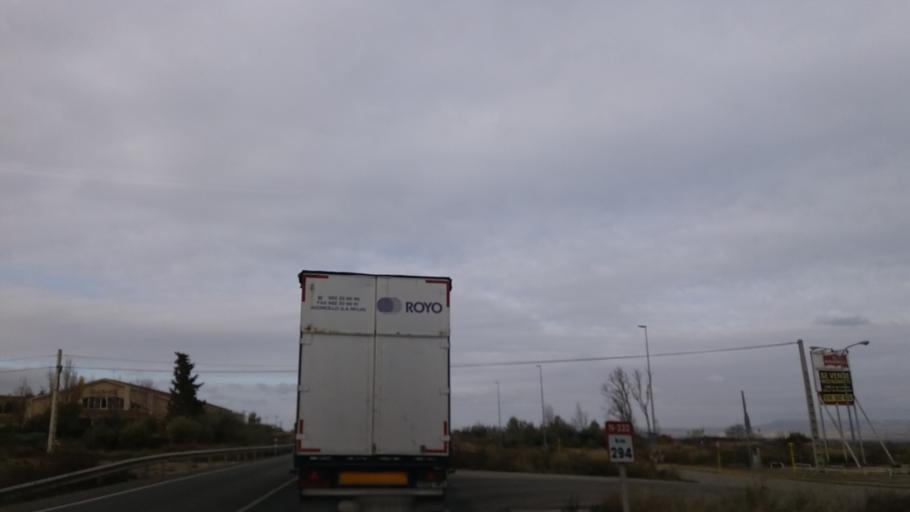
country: ES
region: Aragon
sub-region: Provincia de Zaragoza
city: Mallen
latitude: 41.8995
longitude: -1.4123
